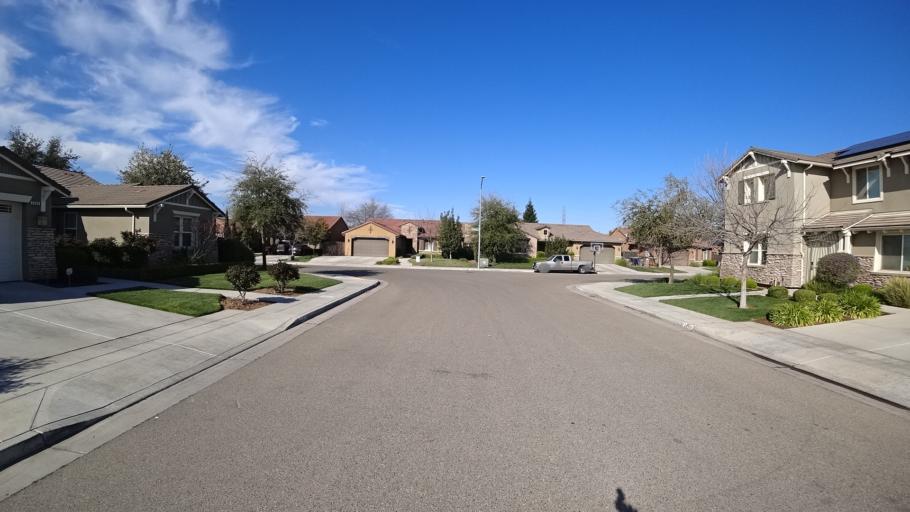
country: US
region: California
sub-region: Fresno County
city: West Park
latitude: 36.7971
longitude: -119.8965
